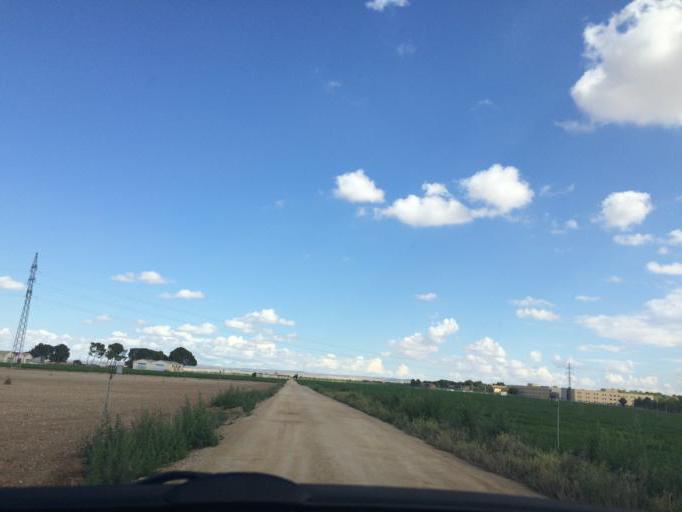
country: ES
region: Castille-La Mancha
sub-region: Provincia de Albacete
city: Albacete
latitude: 38.9586
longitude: -1.8714
